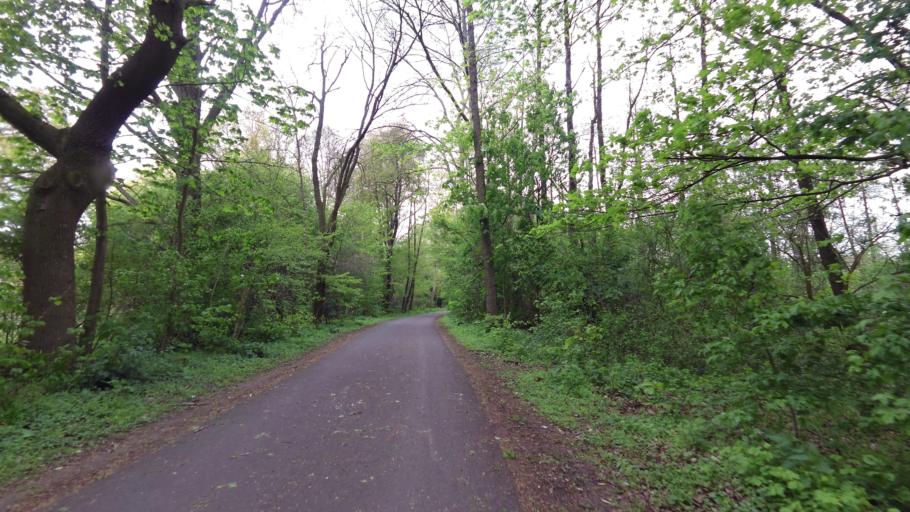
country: DE
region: Lower Saxony
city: Hemmingen
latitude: 52.3315
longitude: 9.7406
